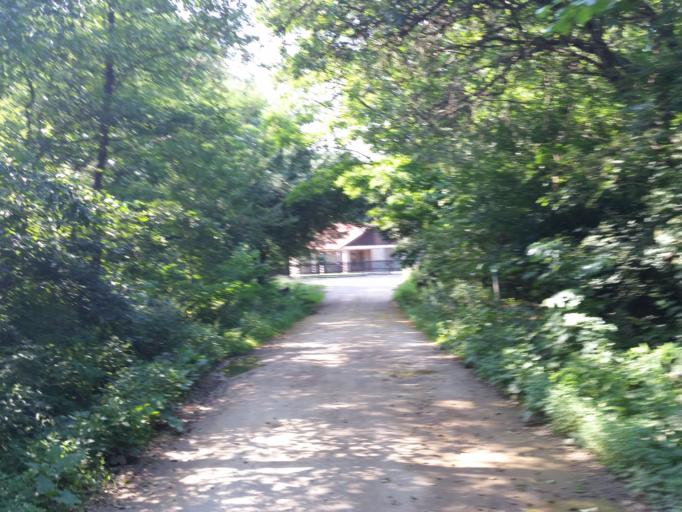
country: HU
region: Vas
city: Sarvar
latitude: 47.1615
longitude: 16.9832
